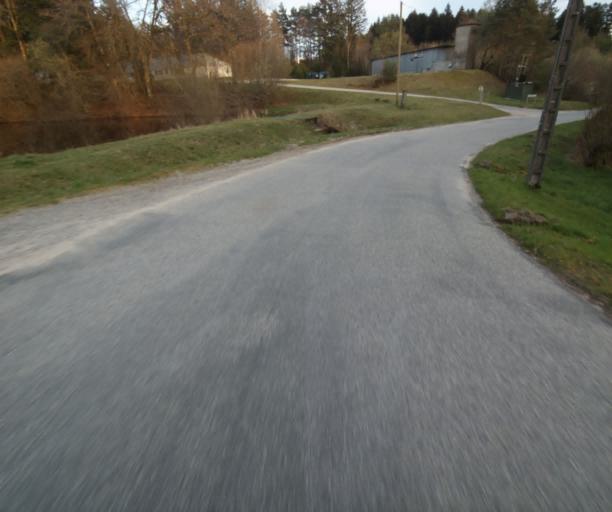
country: FR
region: Limousin
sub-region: Departement de la Correze
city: Correze
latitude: 45.2761
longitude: 1.9745
